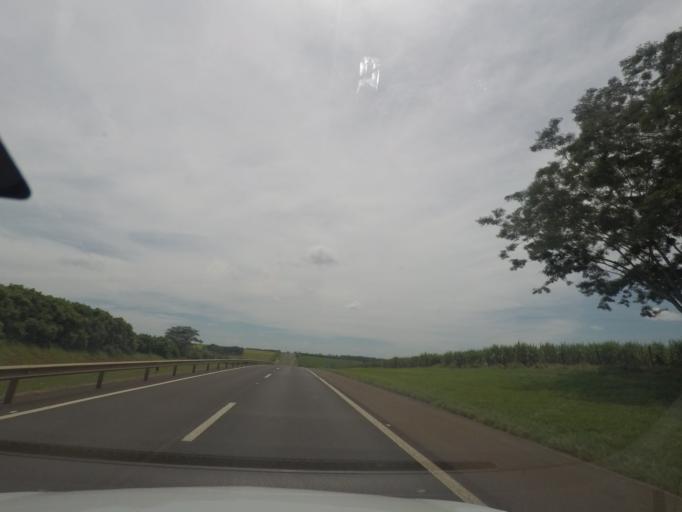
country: BR
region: Sao Paulo
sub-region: Bebedouro
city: Bebedouro
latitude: -21.0219
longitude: -48.4235
